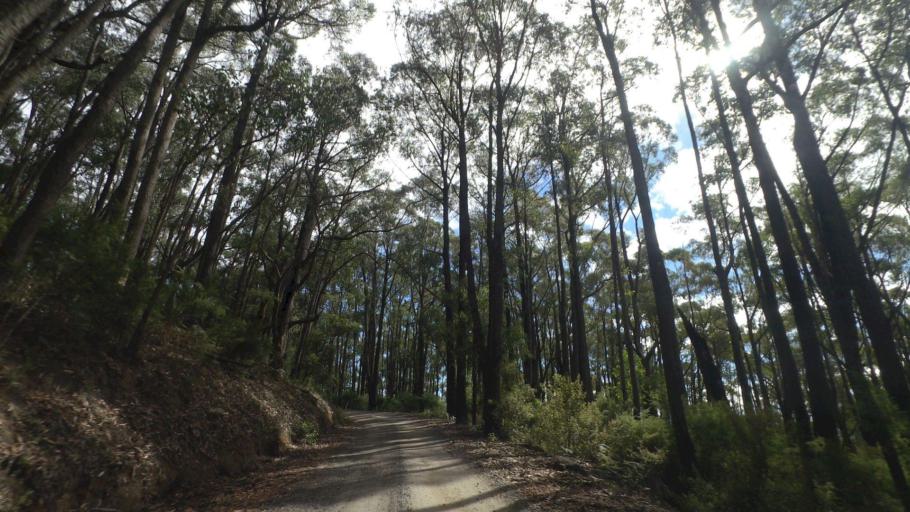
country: AU
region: Victoria
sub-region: Cardinia
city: Gembrook
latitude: -37.9152
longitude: 145.6223
